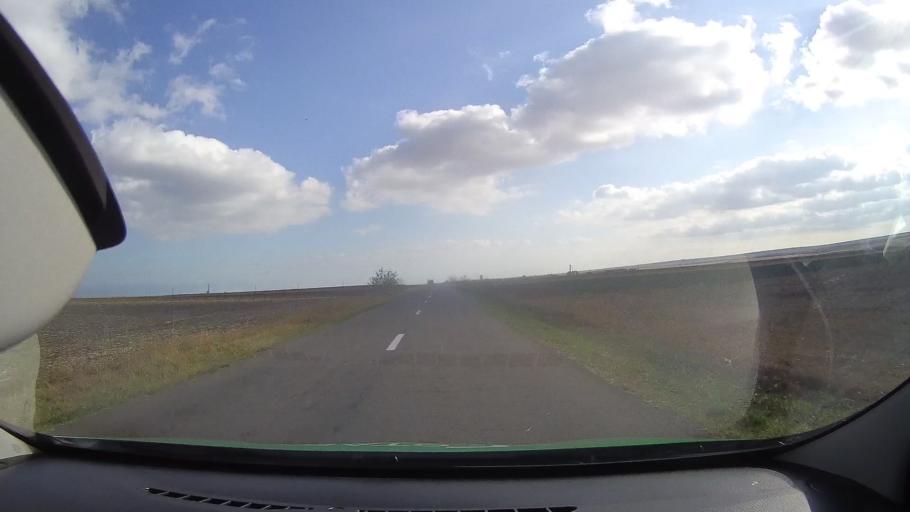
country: RO
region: Constanta
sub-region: Comuna Cogealac
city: Tariverde
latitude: 44.5543
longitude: 28.6206
